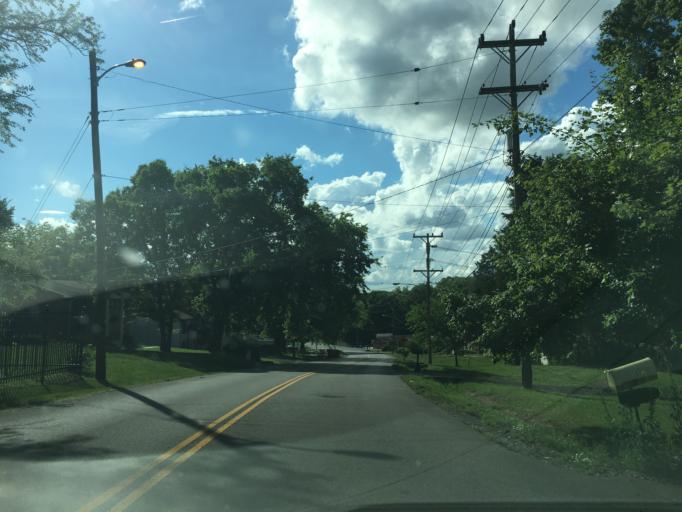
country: US
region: Tennessee
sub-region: Davidson County
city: Oak Hill
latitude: 36.0820
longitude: -86.7213
